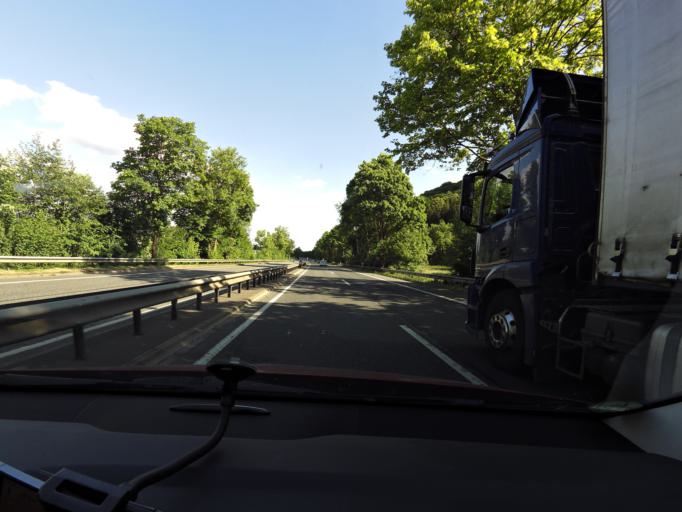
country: DE
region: Rheinland-Pfalz
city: Sinzig
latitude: 50.5332
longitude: 7.2702
